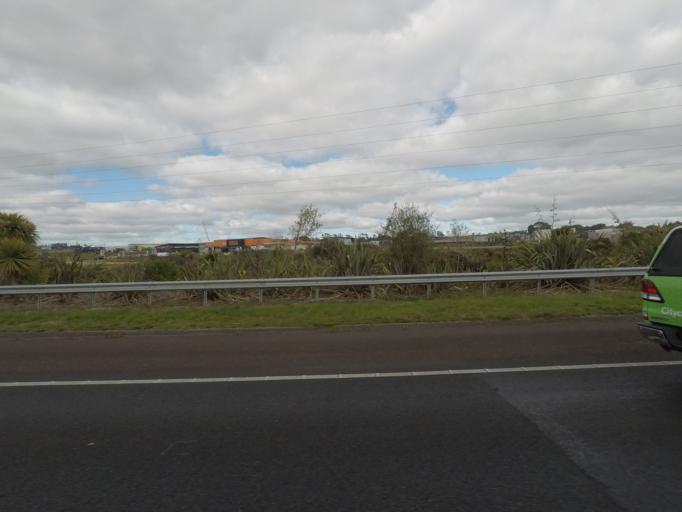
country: NZ
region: Auckland
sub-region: Auckland
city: Rosebank
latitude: -36.8065
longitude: 174.6070
